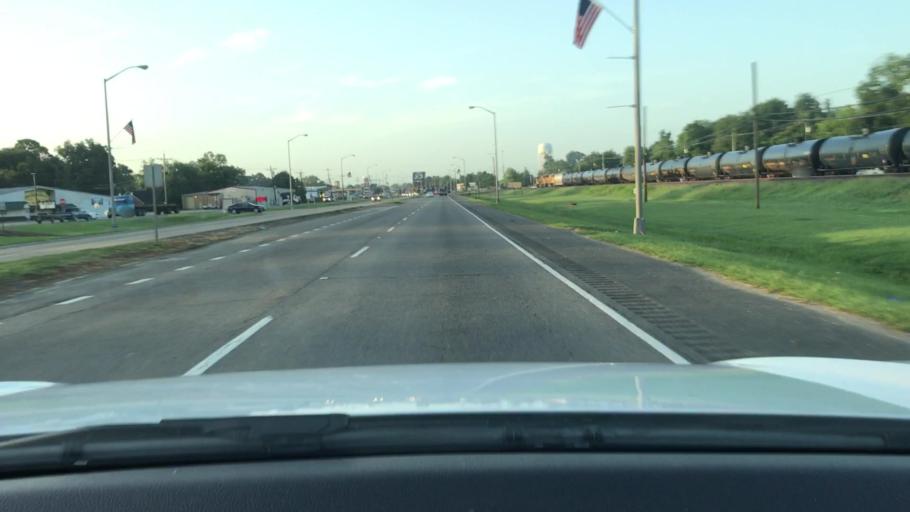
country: US
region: Louisiana
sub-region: Iberville Parish
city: Plaquemine
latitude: 30.3008
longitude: -91.2429
